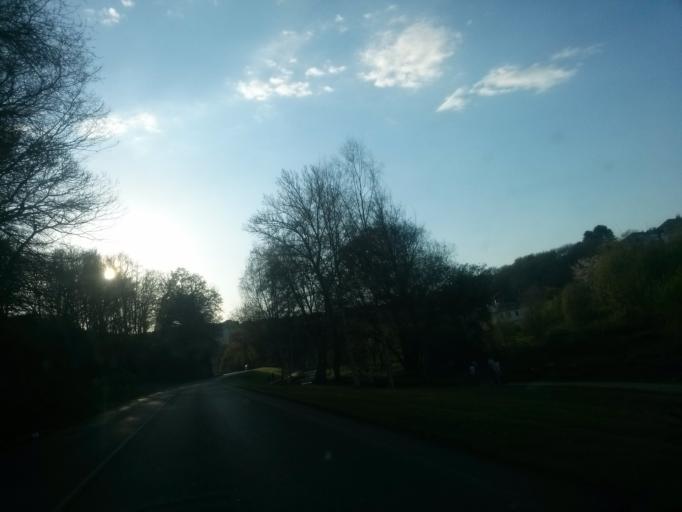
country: ES
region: Galicia
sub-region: Provincia de Lugo
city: Lugo
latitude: 43.0065
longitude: -7.5381
